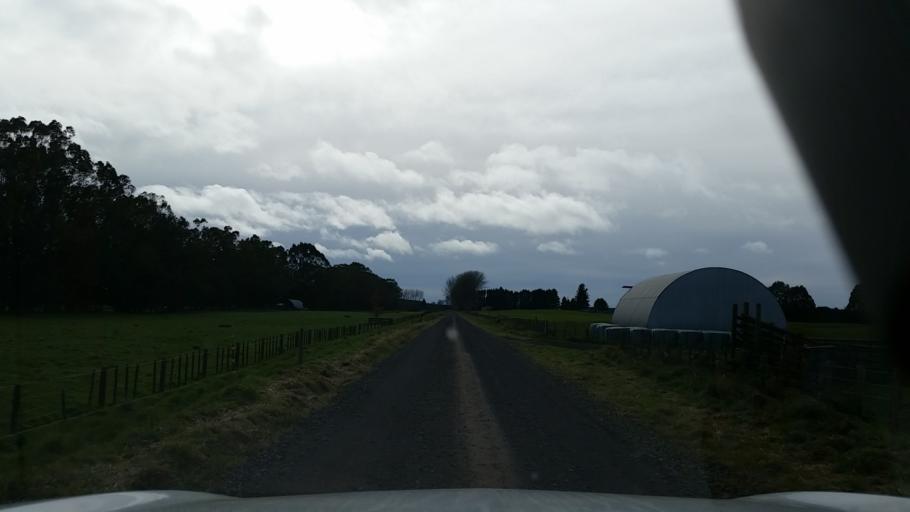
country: NZ
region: Bay of Plenty
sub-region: Whakatane District
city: Murupara
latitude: -38.4782
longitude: 176.4148
